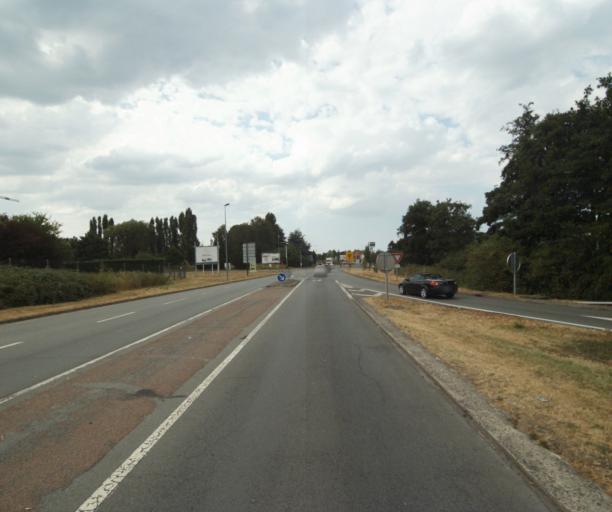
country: FR
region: Nord-Pas-de-Calais
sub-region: Departement du Nord
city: Neuville-en-Ferrain
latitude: 50.7627
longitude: 3.1576
